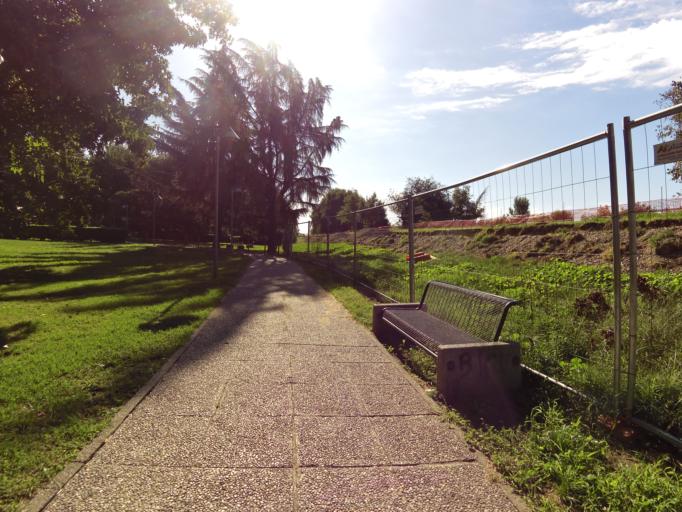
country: IT
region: Lombardy
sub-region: Citta metropolitana di Milano
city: Civesio
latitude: 45.4022
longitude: 9.2687
